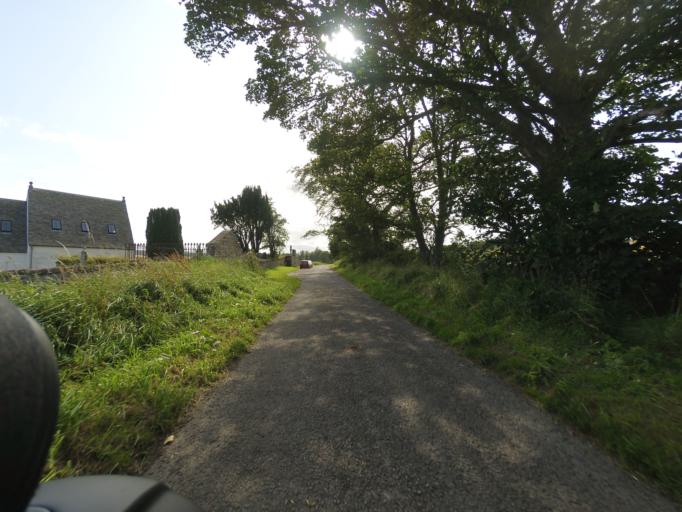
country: GB
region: Scotland
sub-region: Highland
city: Invergordon
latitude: 57.6643
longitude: -4.1708
